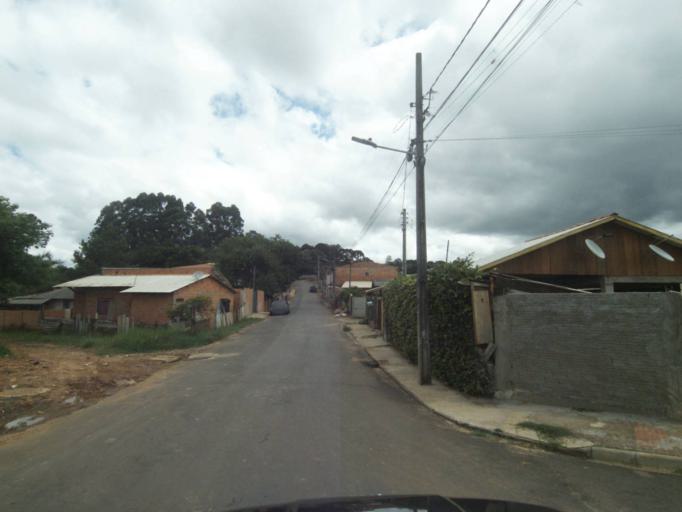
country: BR
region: Parana
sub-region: Telemaco Borba
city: Telemaco Borba
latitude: -24.3173
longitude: -50.6454
